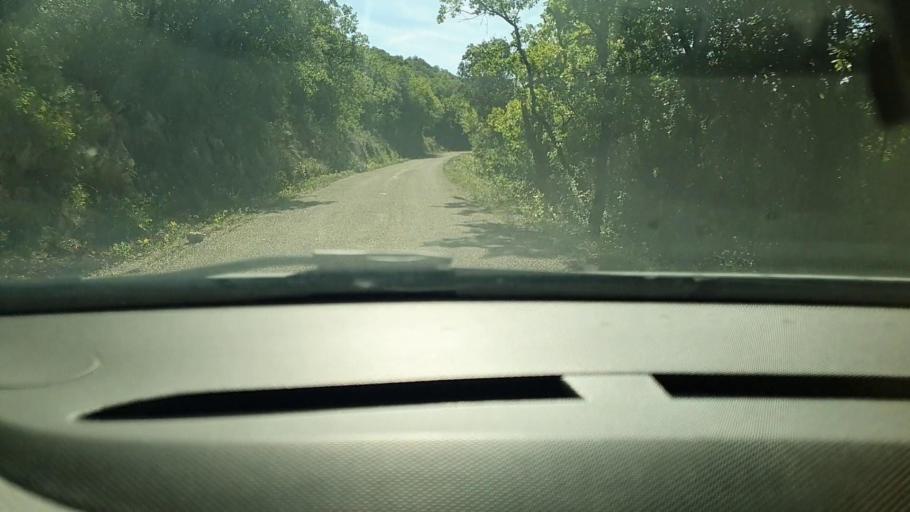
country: FR
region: Languedoc-Roussillon
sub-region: Departement du Gard
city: Barjac
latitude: 44.2028
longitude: 4.3134
